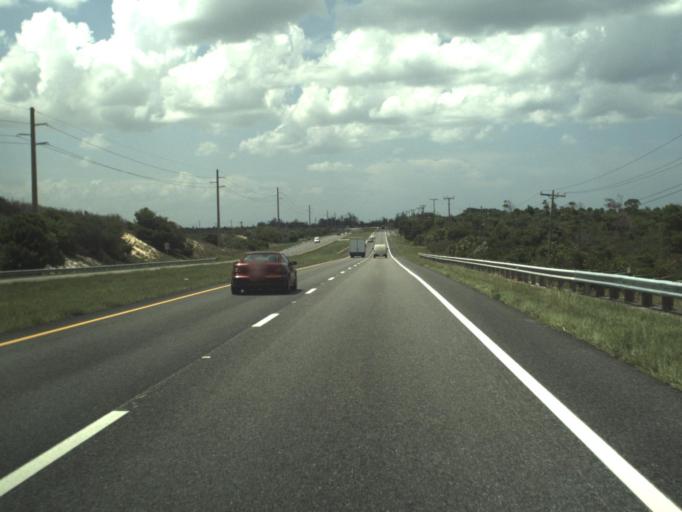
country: US
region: Florida
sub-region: Martin County
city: Hobe Sound
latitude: 27.0316
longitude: -80.1109
